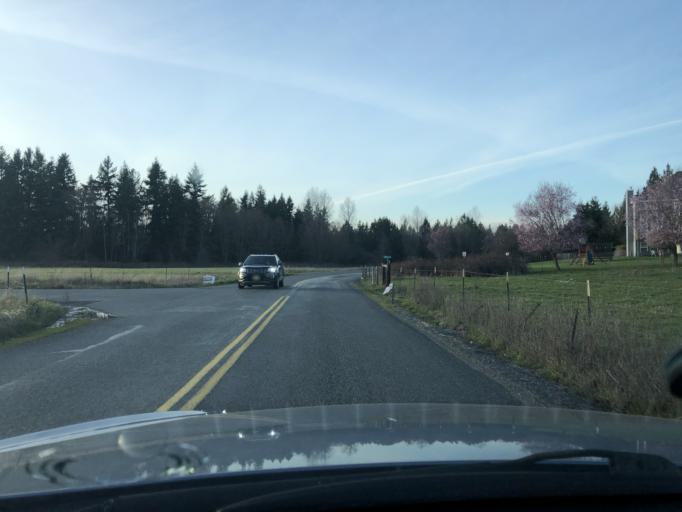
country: US
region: Washington
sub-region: Pierce County
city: Bonney Lake
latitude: 47.2018
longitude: -122.1222
